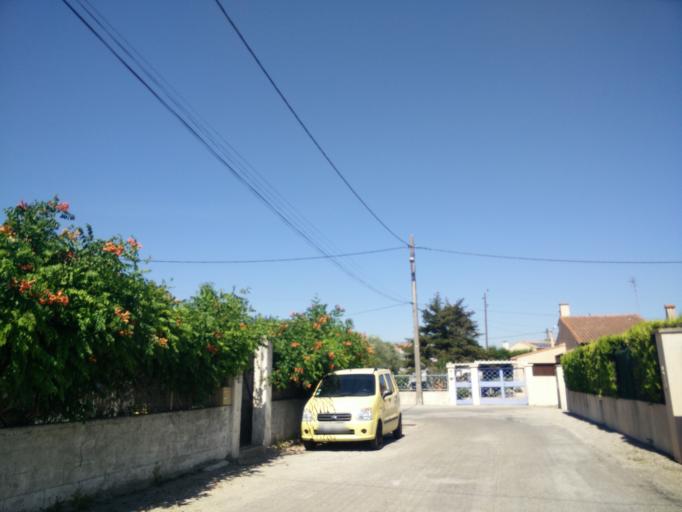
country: FR
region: Languedoc-Roussillon
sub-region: Departement du Gard
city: Vestric-et-Candiac
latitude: 43.7408
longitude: 4.2560
